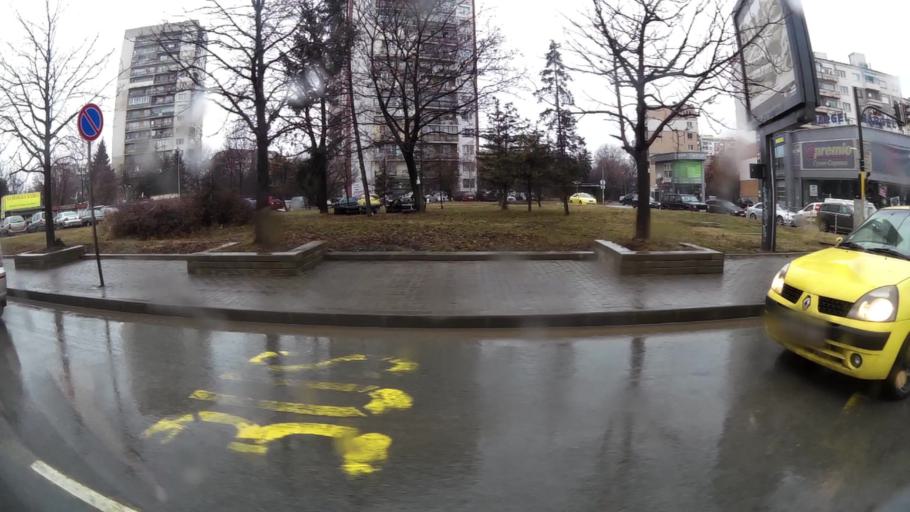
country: BG
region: Sofia-Capital
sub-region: Stolichna Obshtina
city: Sofia
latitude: 42.6534
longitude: 23.3802
